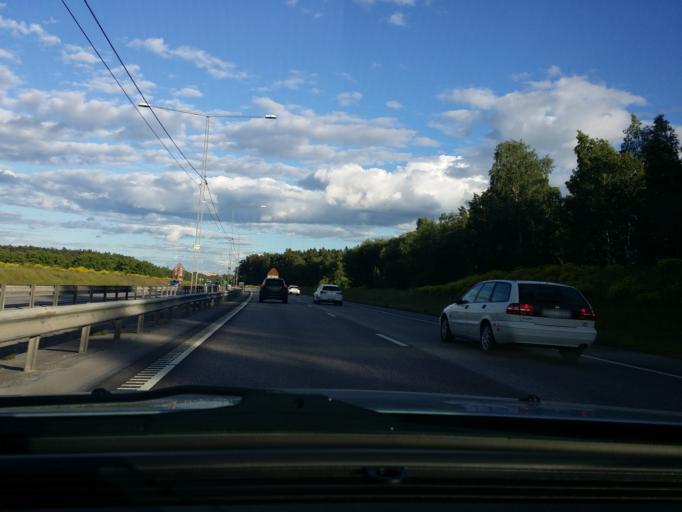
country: SE
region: Stockholm
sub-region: Upplands Vasby Kommun
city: Upplands Vaesby
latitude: 59.5374
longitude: 17.9102
